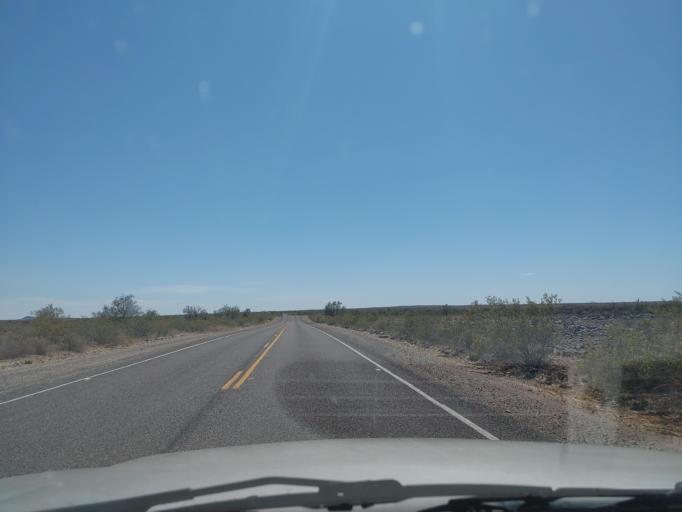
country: US
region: Arizona
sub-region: Maricopa County
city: Gila Bend
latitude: 32.9198
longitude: -113.2845
